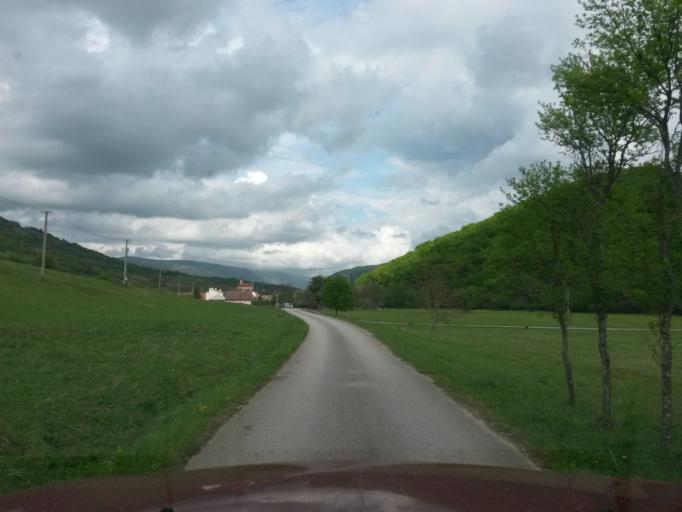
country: SK
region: Kosicky
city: Roznava
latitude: 48.5546
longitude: 20.6009
